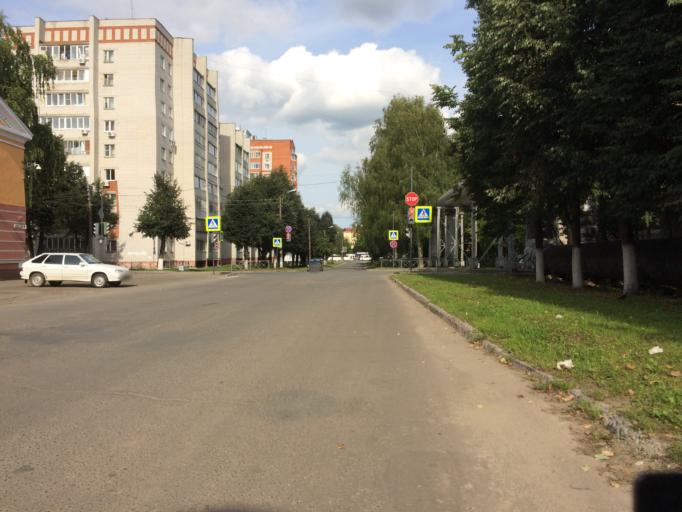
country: RU
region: Mariy-El
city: Yoshkar-Ola
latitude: 56.6314
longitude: 47.8755
